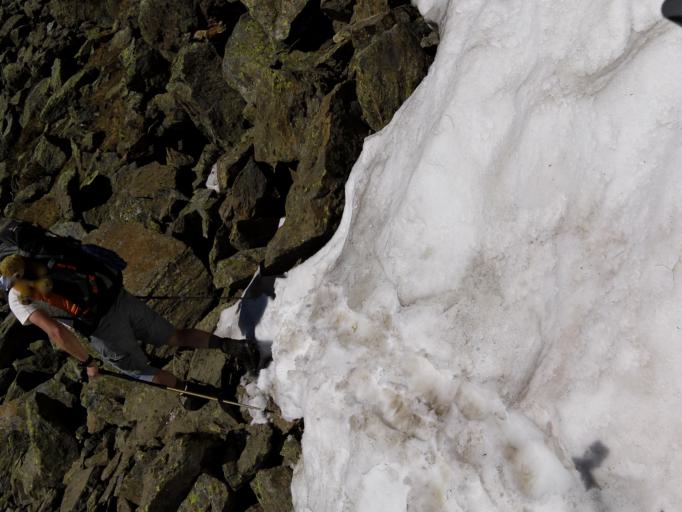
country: AT
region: Tyrol
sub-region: Politischer Bezirk Innsbruck Land
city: Sellrain
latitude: 47.1294
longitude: 11.2276
